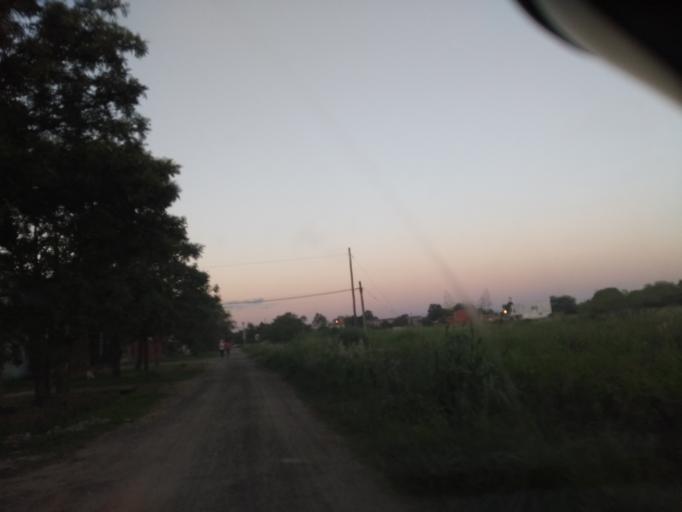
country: AR
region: Chaco
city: Fontana
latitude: -27.4206
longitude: -59.0429
